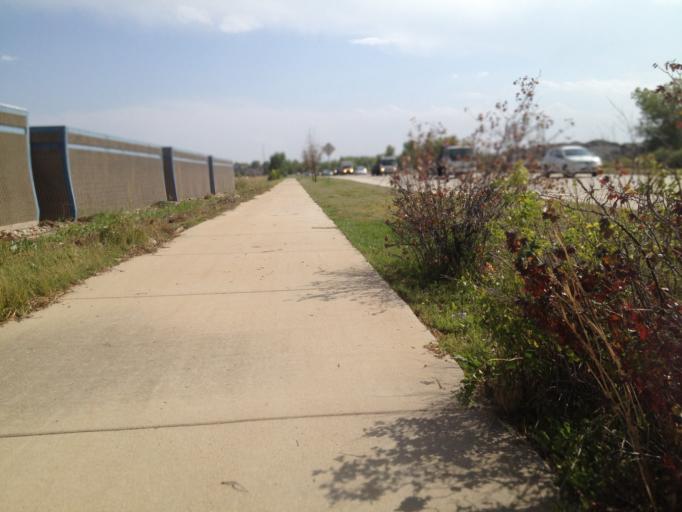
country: US
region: Colorado
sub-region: Boulder County
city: Lafayette
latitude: 39.9843
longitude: -105.0982
